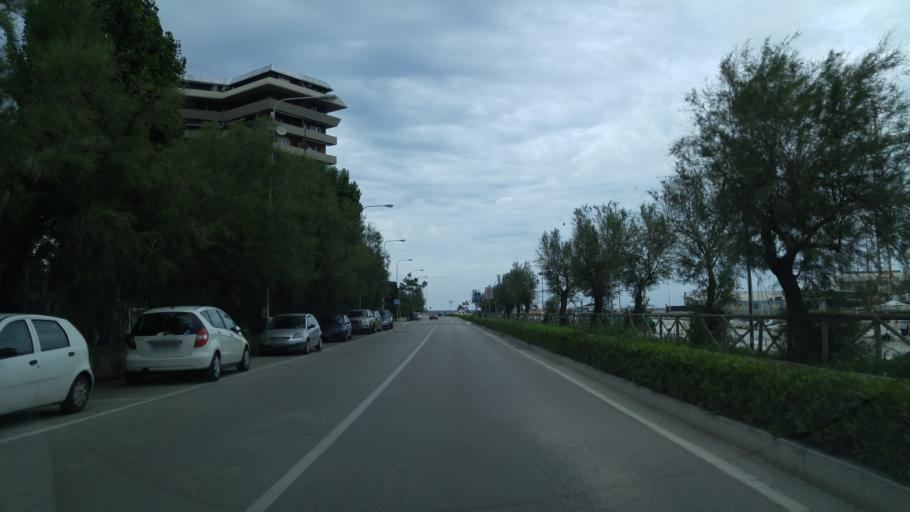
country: IT
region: The Marches
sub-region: Provincia di Pesaro e Urbino
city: Pesaro
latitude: 43.9207
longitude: 12.9023
